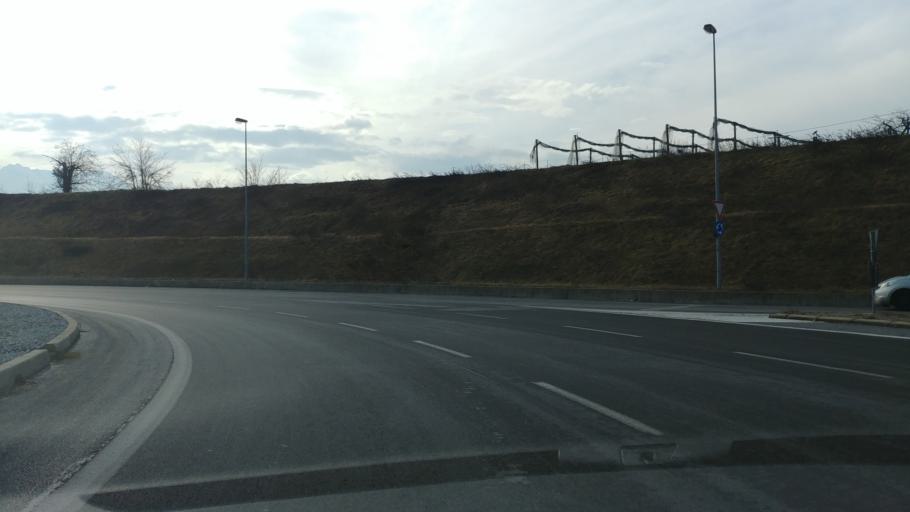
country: IT
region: Piedmont
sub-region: Provincia di Cuneo
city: Cuneo
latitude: 44.3879
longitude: 7.5197
